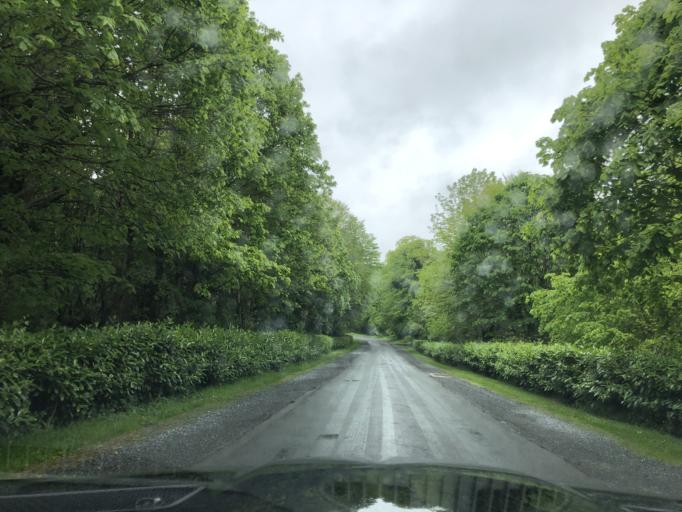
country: GB
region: Northern Ireland
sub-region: Down District
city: Portaferry
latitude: 54.3610
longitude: -5.5792
